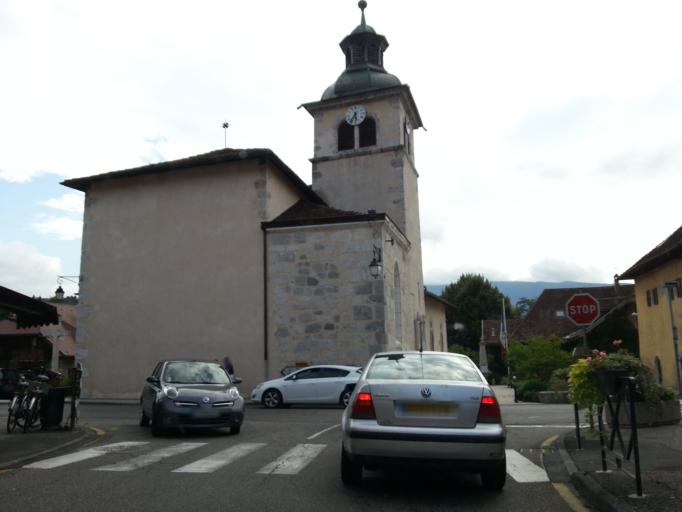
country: FR
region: Rhone-Alpes
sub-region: Departement de la Haute-Savoie
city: Menthon-Saint-Bernard
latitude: 45.8600
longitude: 6.1962
